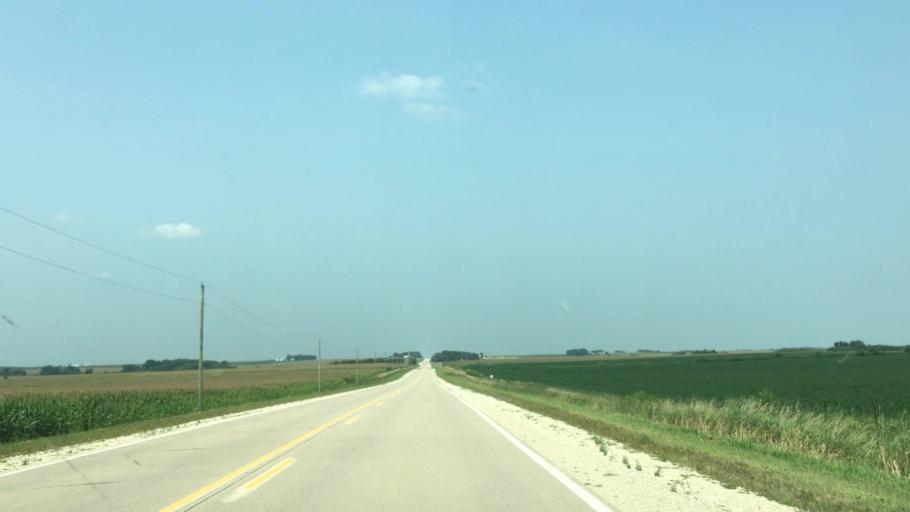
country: US
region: Iowa
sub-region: Fayette County
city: Fayette
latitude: 42.7456
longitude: -91.8041
